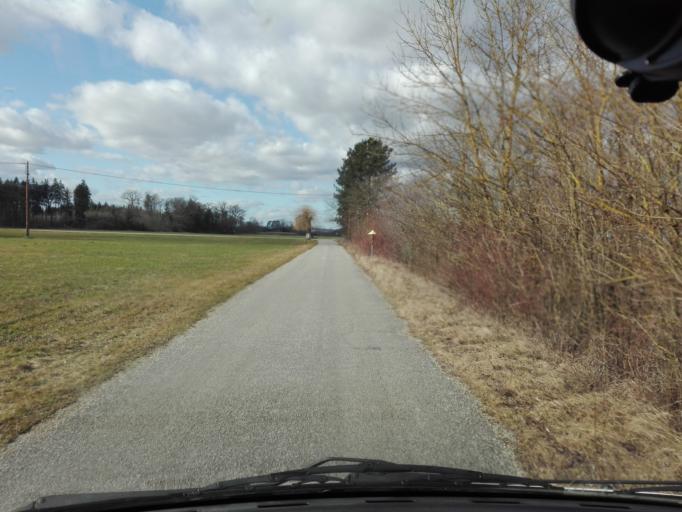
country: AT
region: Upper Austria
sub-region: Politischer Bezirk Perg
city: Perg
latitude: 48.2074
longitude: 14.6841
